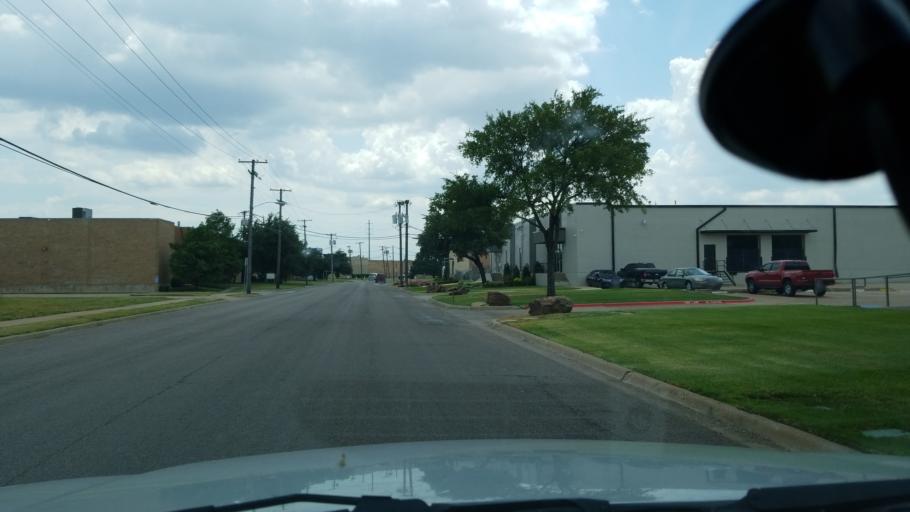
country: US
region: Texas
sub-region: Dallas County
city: Irving
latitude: 32.8334
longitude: -96.8838
